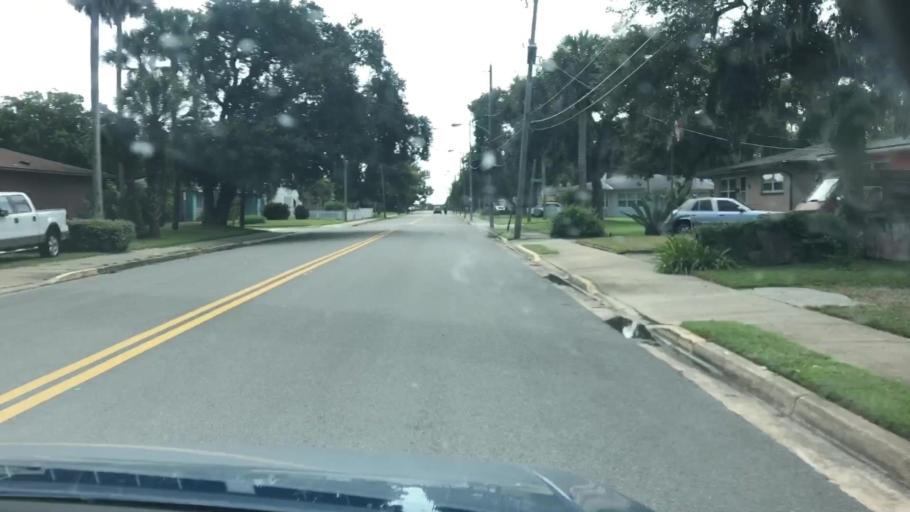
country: US
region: Florida
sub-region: Volusia County
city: Daytona Beach
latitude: 29.1969
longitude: -81.0127
